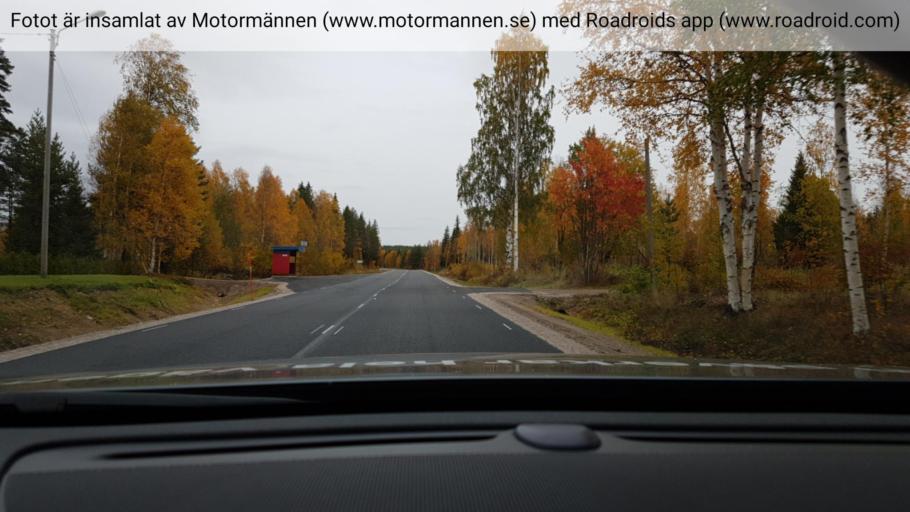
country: SE
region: Norrbotten
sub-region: Overkalix Kommun
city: OEverkalix
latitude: 66.3697
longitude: 22.8433
